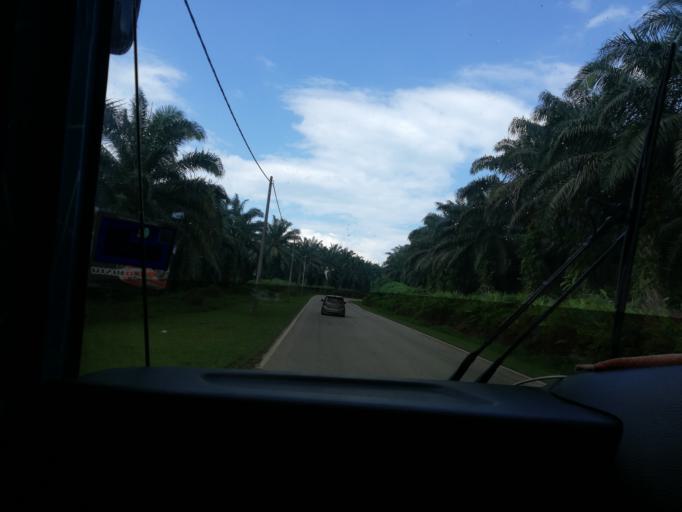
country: MY
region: Kedah
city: Kulim
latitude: 5.2662
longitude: 100.6091
